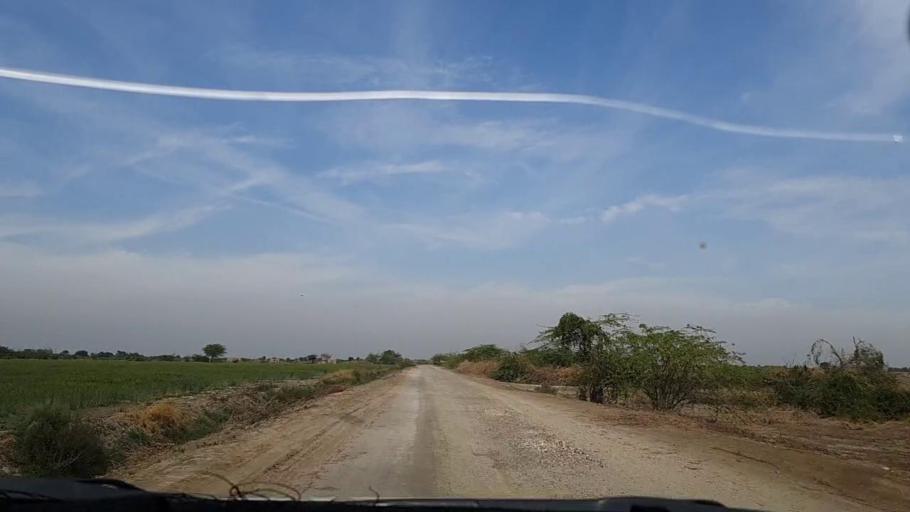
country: PK
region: Sindh
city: Pithoro
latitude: 25.4721
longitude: 69.4570
